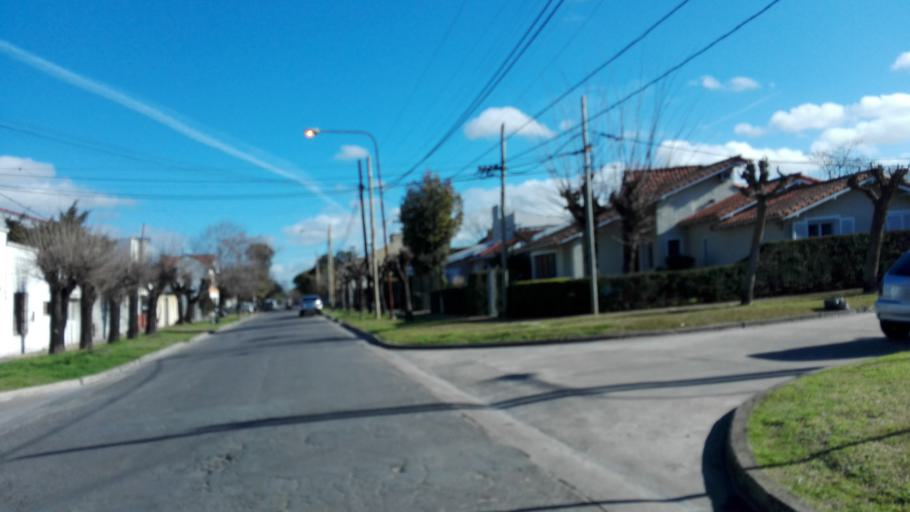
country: AR
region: Buenos Aires
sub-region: Partido de La Plata
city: La Plata
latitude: -34.8856
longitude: -57.9976
